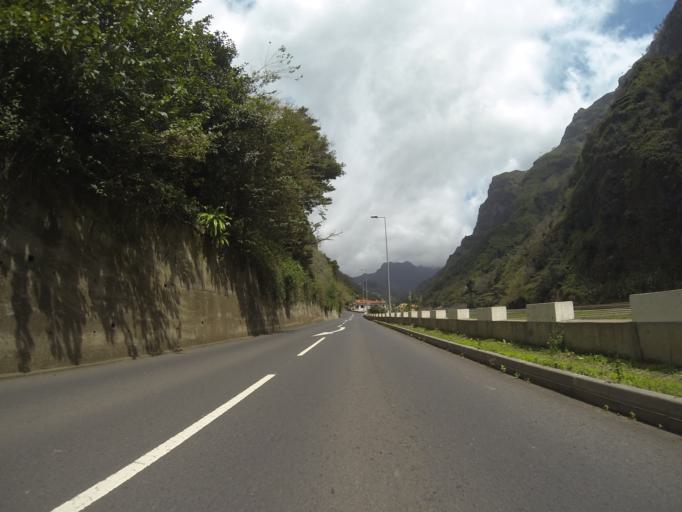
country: PT
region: Madeira
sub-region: Ribeira Brava
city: Campanario
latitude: 32.7107
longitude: -17.0359
